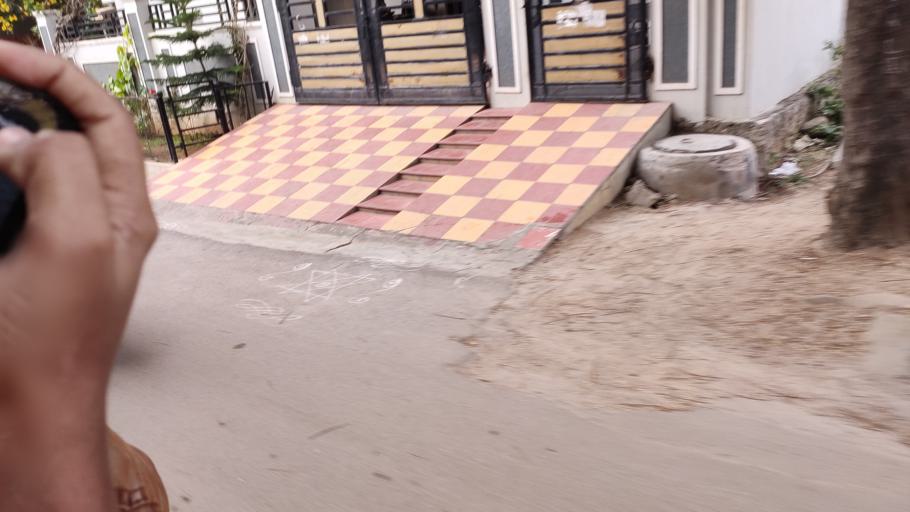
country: IN
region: Telangana
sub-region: Rangareddi
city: Kukatpalli
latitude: 17.4928
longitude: 78.3882
